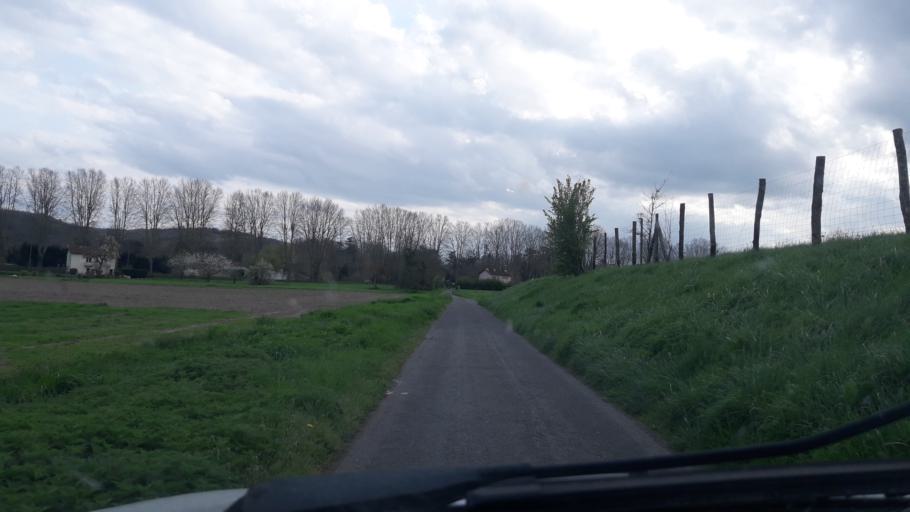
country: FR
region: Midi-Pyrenees
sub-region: Departement de la Haute-Garonne
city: Carbonne
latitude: 43.2947
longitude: 1.2202
